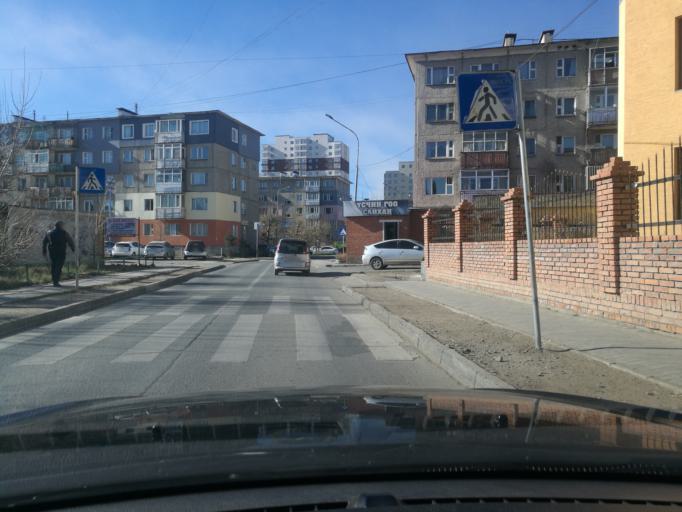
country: MN
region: Ulaanbaatar
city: Ulaanbaatar
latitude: 47.9019
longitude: 106.9034
